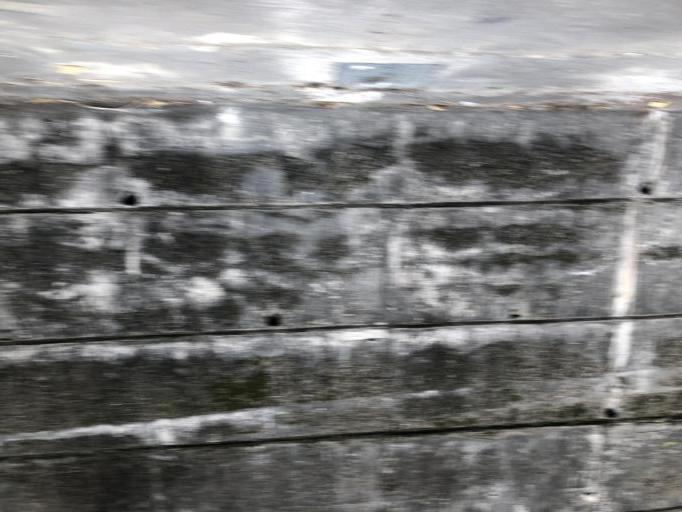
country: TW
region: Taiwan
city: Daxi
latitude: 24.6798
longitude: 121.3822
